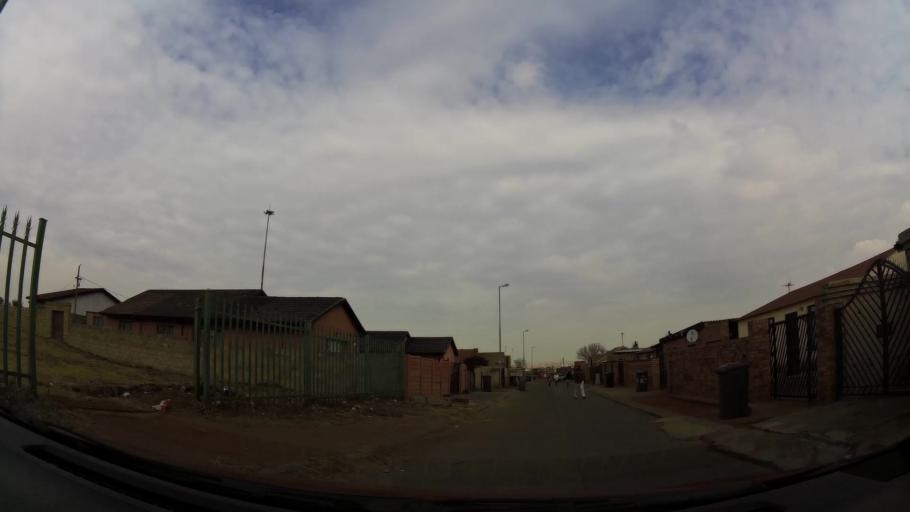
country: ZA
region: Gauteng
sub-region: City of Johannesburg Metropolitan Municipality
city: Soweto
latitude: -26.2549
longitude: 27.8163
